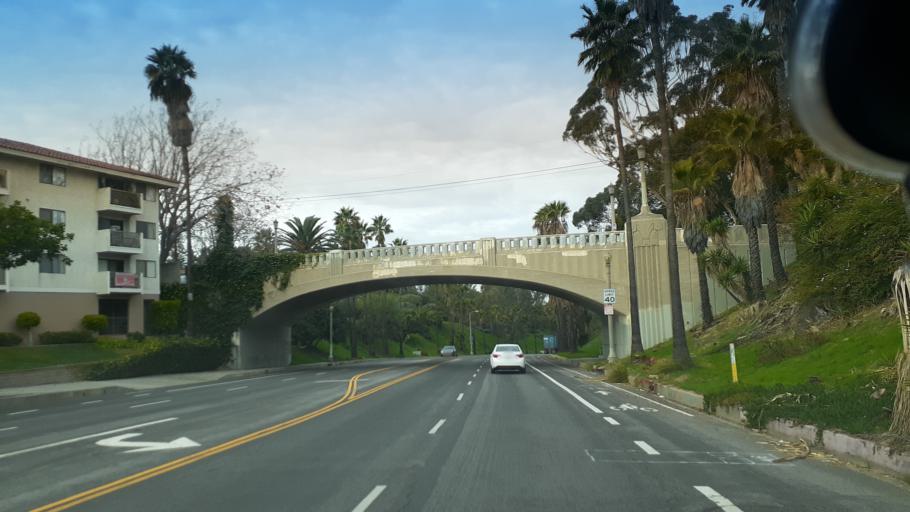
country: US
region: California
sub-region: Los Angeles County
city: San Pedro
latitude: 33.7477
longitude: -118.2931
